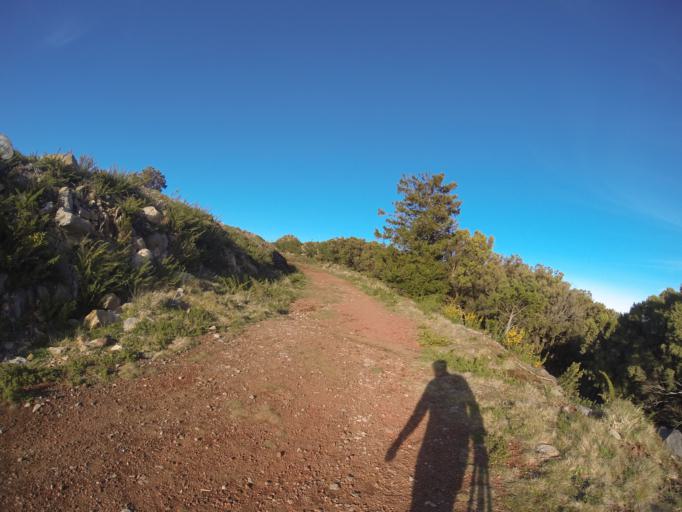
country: PT
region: Madeira
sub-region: Sao Vicente
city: Sao Vicente
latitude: 32.7555
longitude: -17.0573
